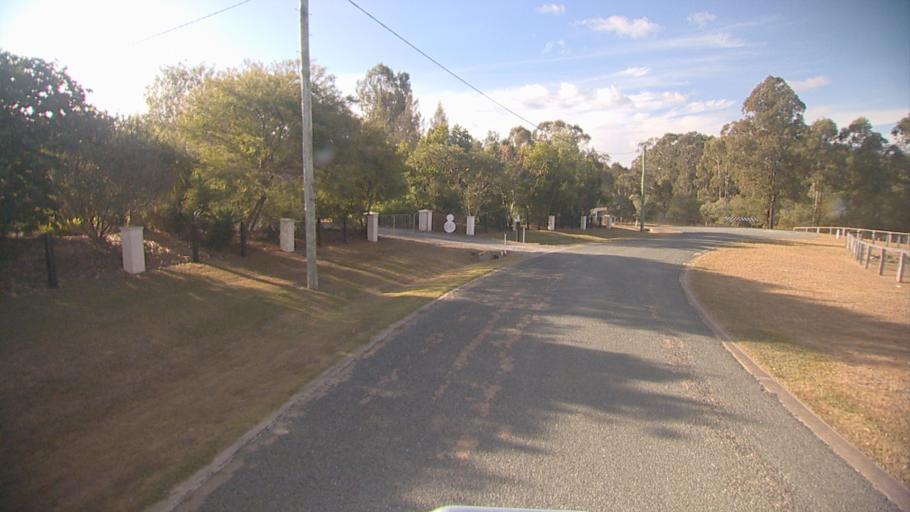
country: AU
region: Queensland
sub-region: Logan
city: Cedar Vale
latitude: -27.8866
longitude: 153.0094
